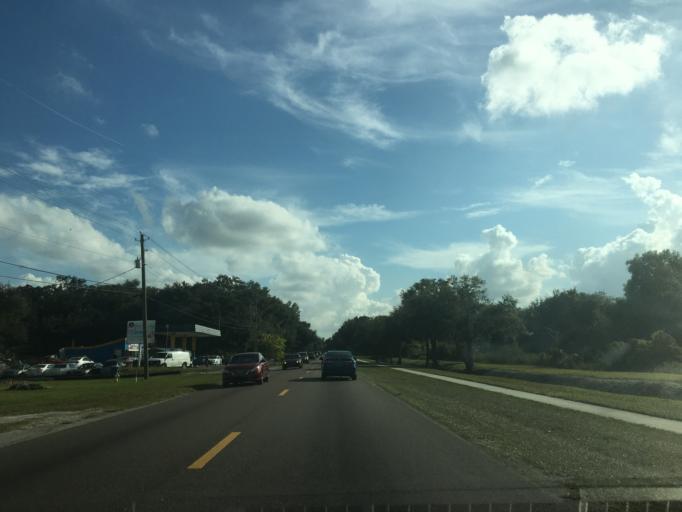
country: US
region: Florida
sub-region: Hillsborough County
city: Temple Terrace
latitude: 28.0153
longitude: -82.4315
